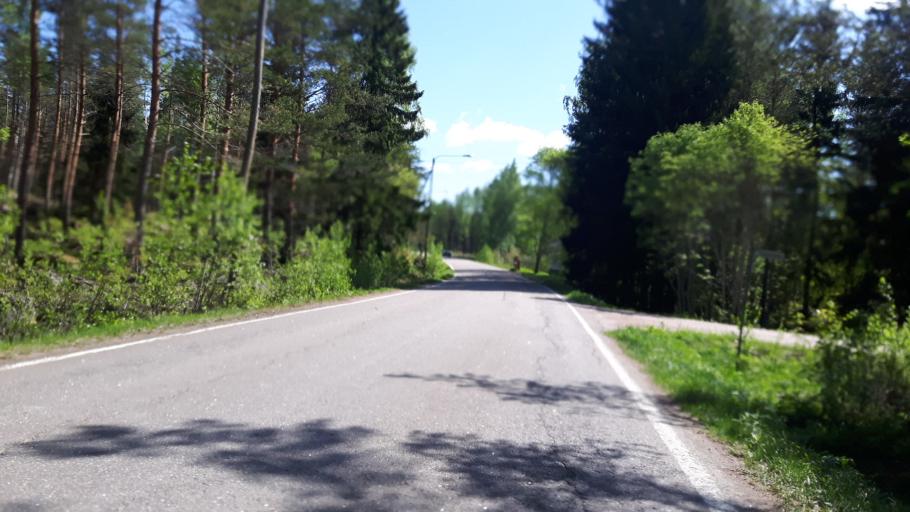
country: FI
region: Kymenlaakso
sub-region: Kotka-Hamina
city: Hamina
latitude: 60.5134
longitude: 27.4336
